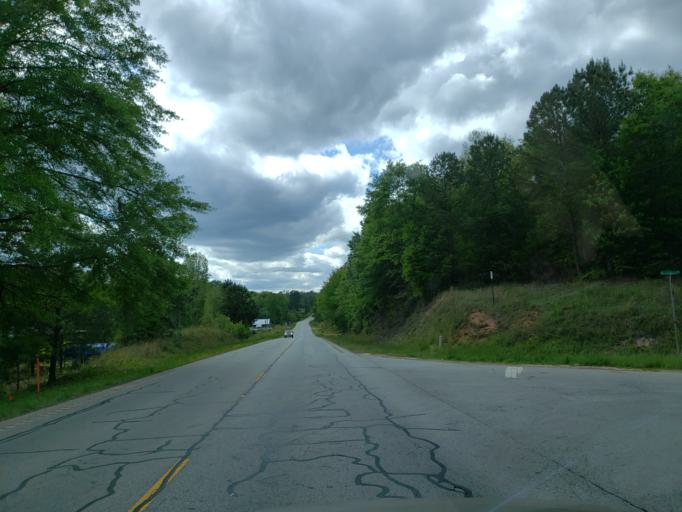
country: US
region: Georgia
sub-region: Haralson County
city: Tallapoosa
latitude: 33.7457
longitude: -85.3479
